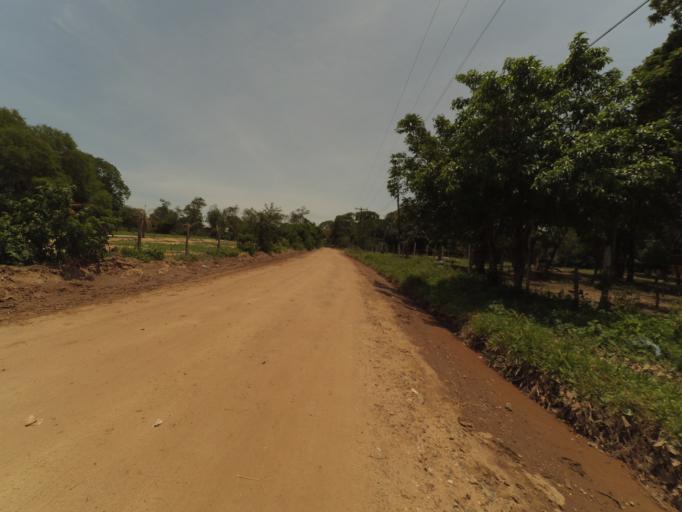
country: BO
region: Santa Cruz
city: Santa Cruz de la Sierra
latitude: -17.8281
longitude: -63.2525
